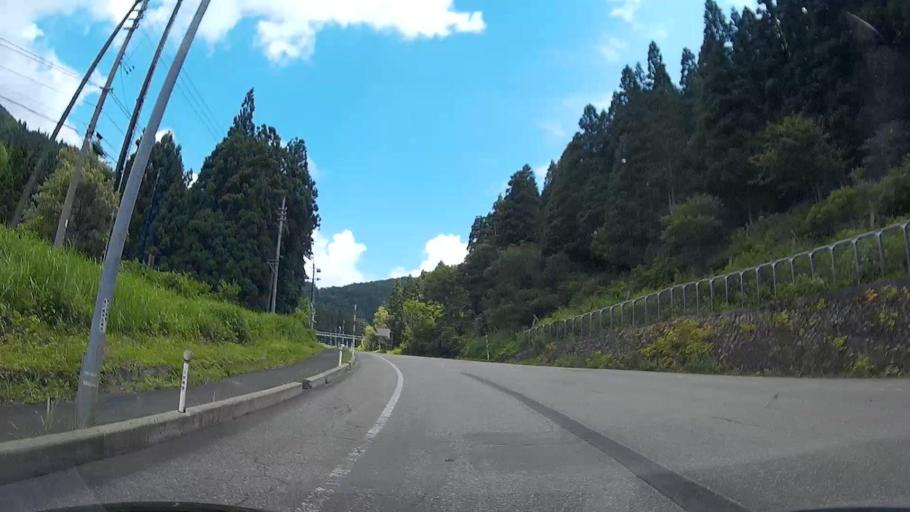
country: JP
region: Niigata
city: Shiozawa
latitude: 36.9043
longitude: 138.7833
